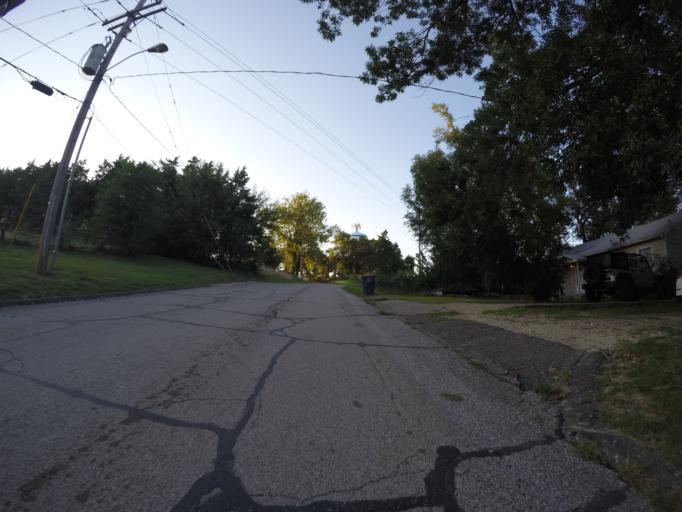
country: US
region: Kansas
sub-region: Riley County
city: Ogden
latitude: 39.1168
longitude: -96.7137
